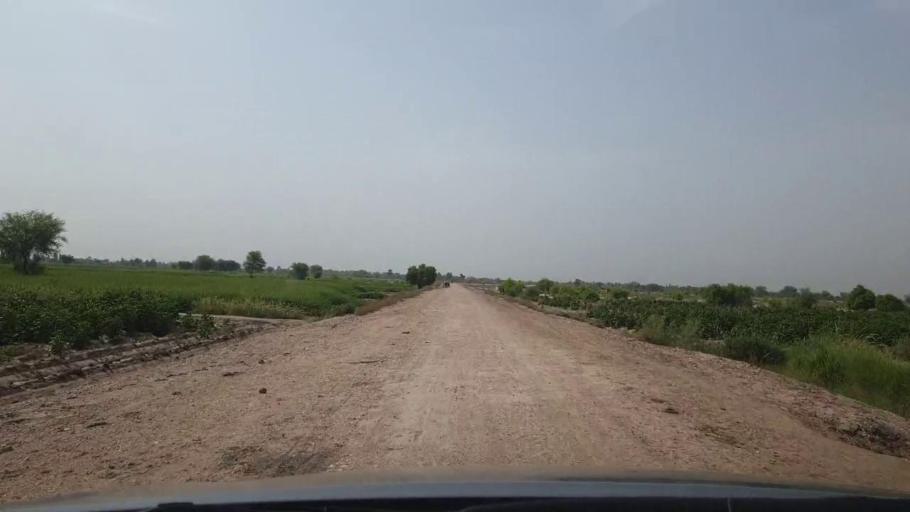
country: PK
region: Sindh
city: Rohri
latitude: 27.6717
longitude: 69.0131
